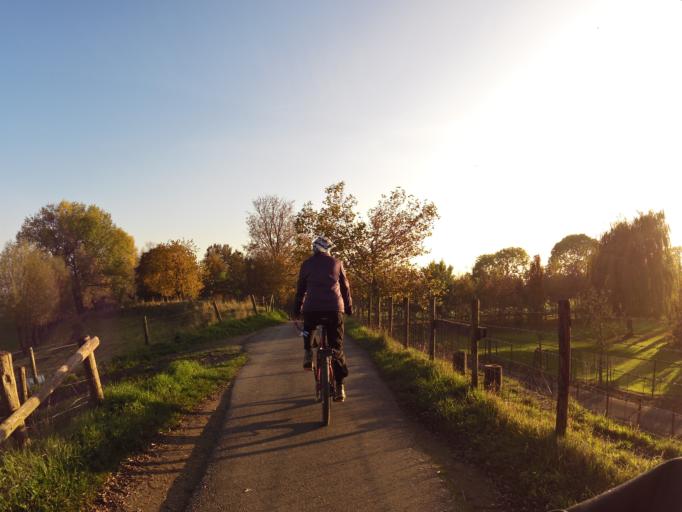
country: NL
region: Gelderland
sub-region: Gemeente Zaltbommel
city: Nederhemert-Noord
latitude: 51.7388
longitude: 5.1839
